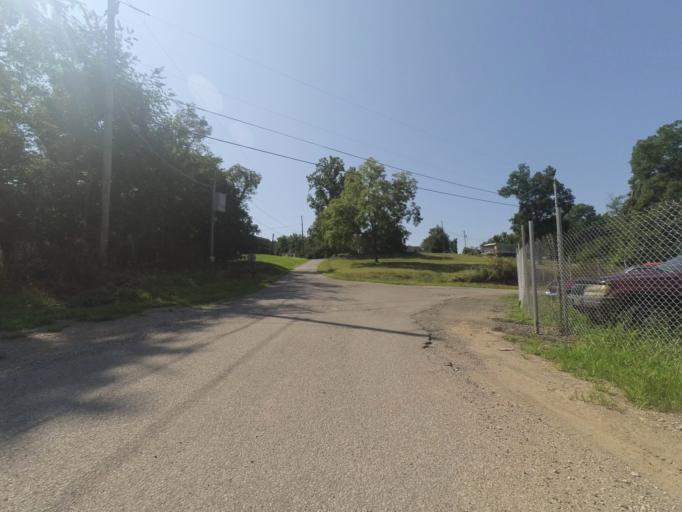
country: US
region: West Virginia
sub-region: Cabell County
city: Huntington
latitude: 38.4346
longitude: -82.4464
